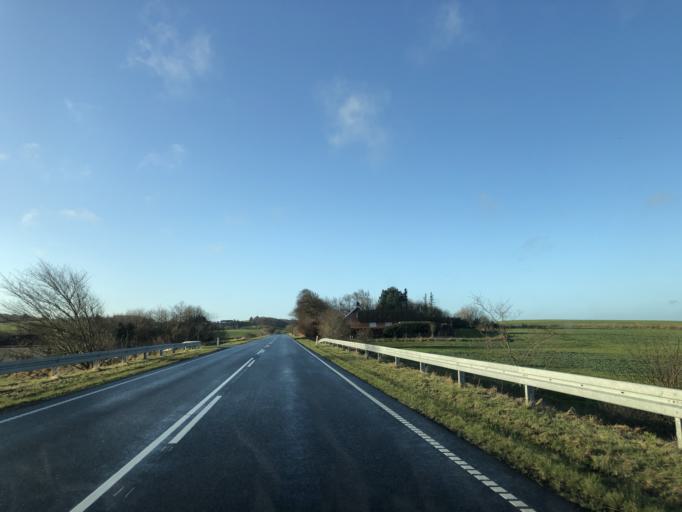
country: DK
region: Central Jutland
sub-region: Lemvig Kommune
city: Lemvig
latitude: 56.5591
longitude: 8.4526
